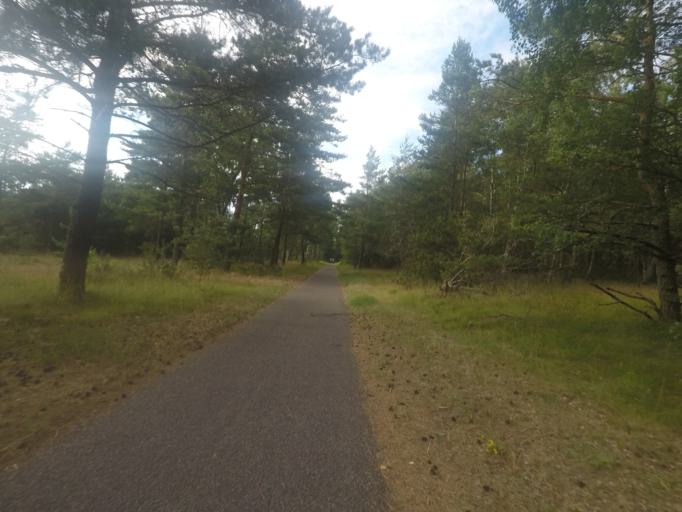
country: LT
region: Klaipedos apskritis
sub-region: Klaipeda
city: Klaipeda
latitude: 55.6726
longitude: 21.1056
